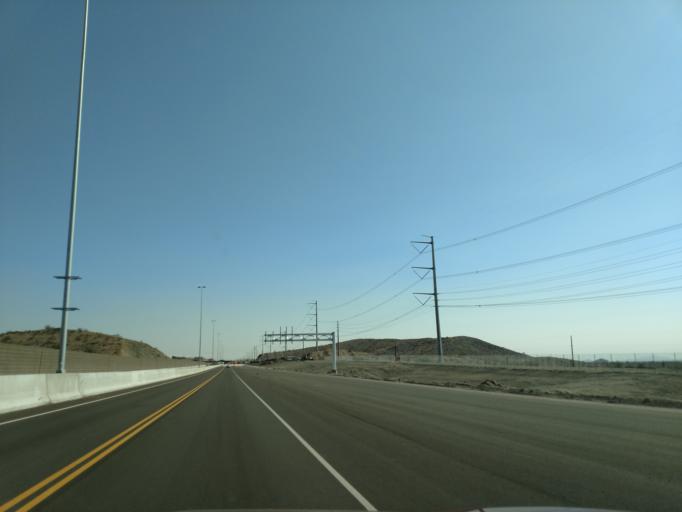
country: US
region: Arizona
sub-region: Maricopa County
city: Laveen
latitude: 33.2913
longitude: -112.0794
